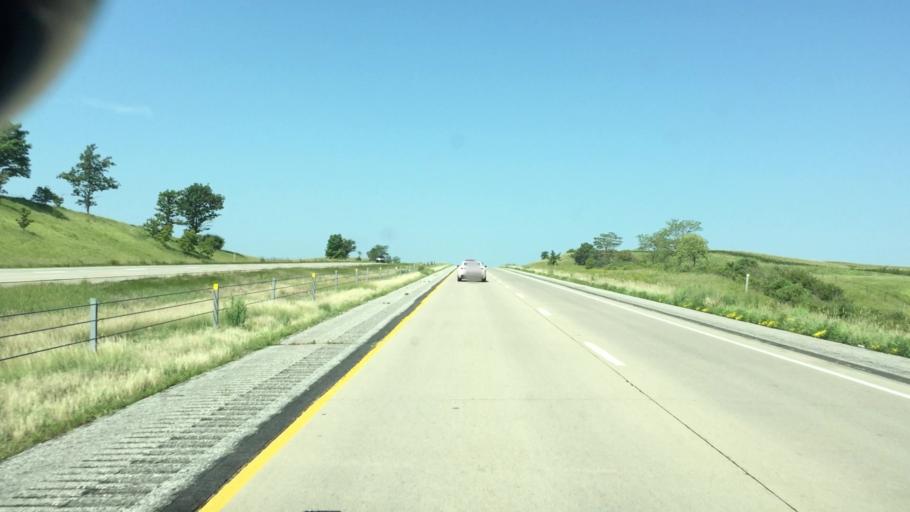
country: US
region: Iowa
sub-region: Iowa County
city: Williamsburg
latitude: 41.6907
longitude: -92.0861
